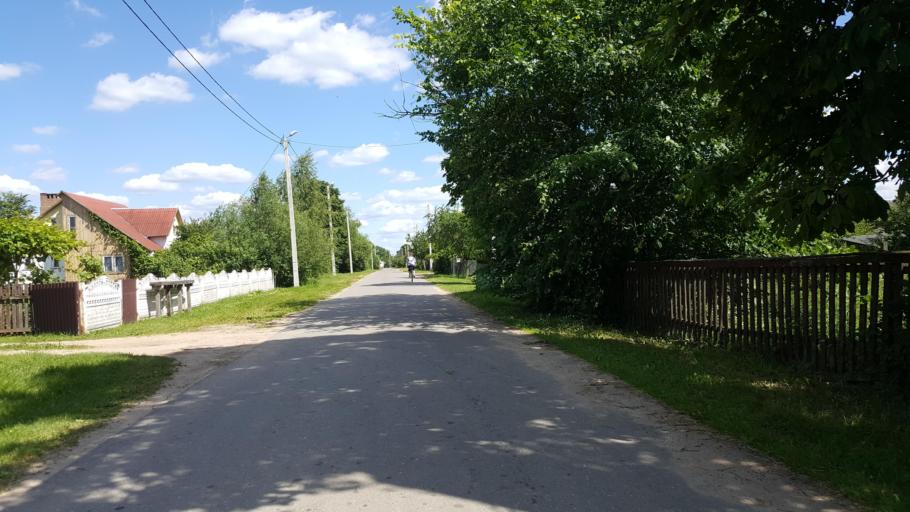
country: PL
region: Podlasie
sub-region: Powiat hajnowski
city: Czeremcha
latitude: 52.5357
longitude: 23.5560
